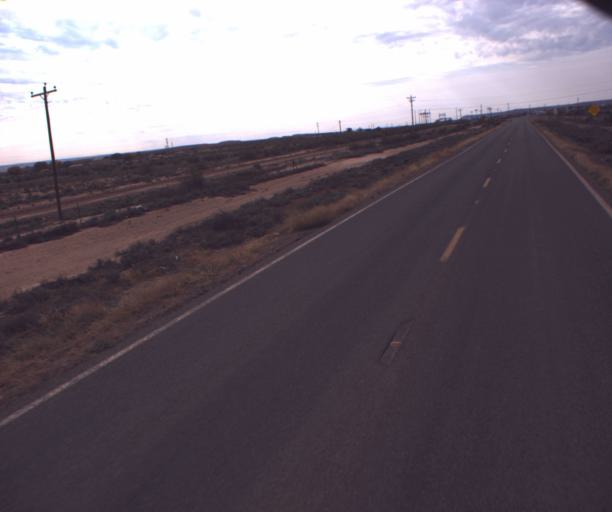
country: US
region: Arizona
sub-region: Apache County
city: Many Farms
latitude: 36.3688
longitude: -109.6134
